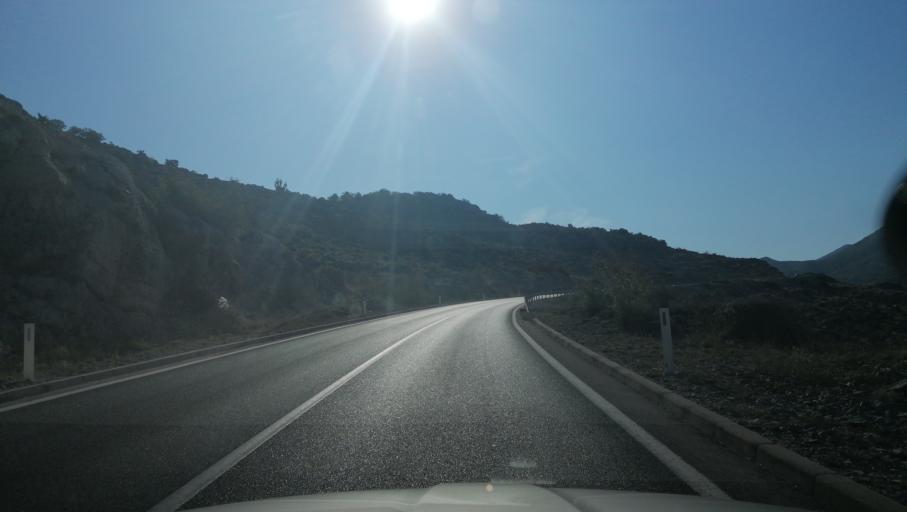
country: BA
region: Republika Srpska
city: Trebinje
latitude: 42.6745
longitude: 18.3447
